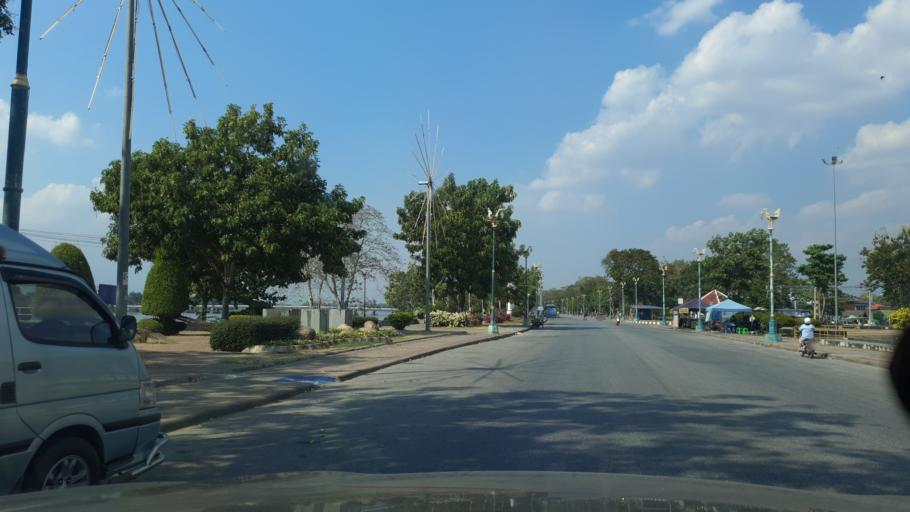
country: TH
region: Tak
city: Tak
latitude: 16.8779
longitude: 99.1209
